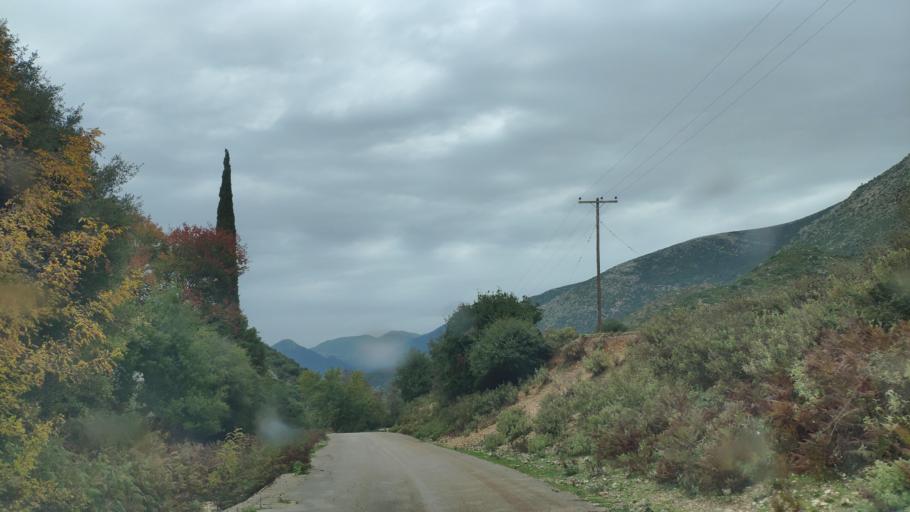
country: GR
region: Epirus
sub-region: Nomos Prevezis
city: Kanalaki
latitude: 39.3621
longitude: 20.6404
